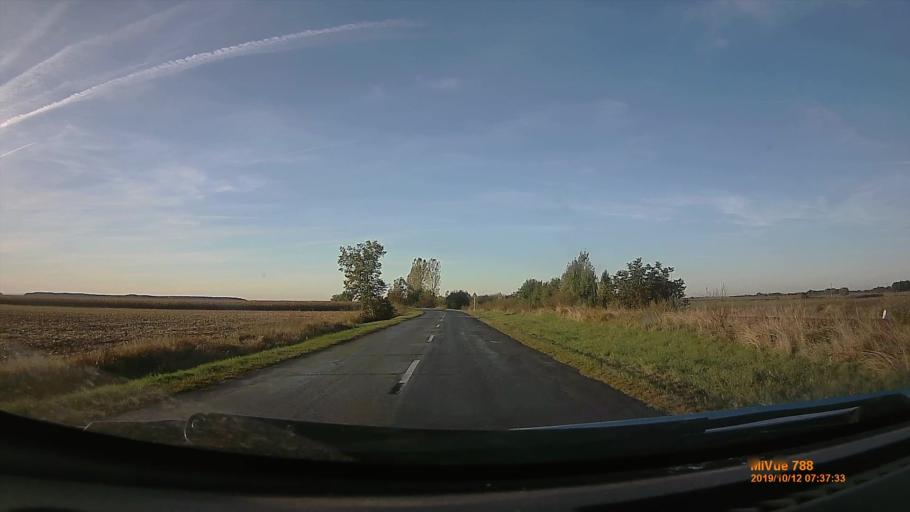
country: HU
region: Hajdu-Bihar
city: Pocsaj
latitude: 47.2351
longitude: 21.8138
